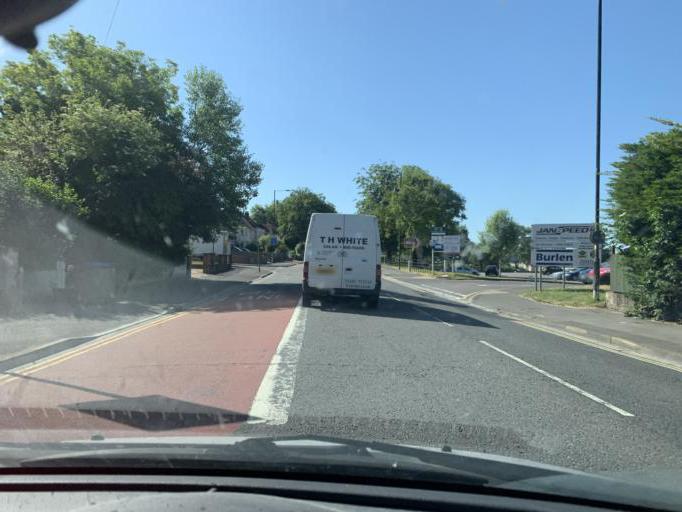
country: GB
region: England
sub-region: Wiltshire
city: Salisbury
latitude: 51.0876
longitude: -1.7986
